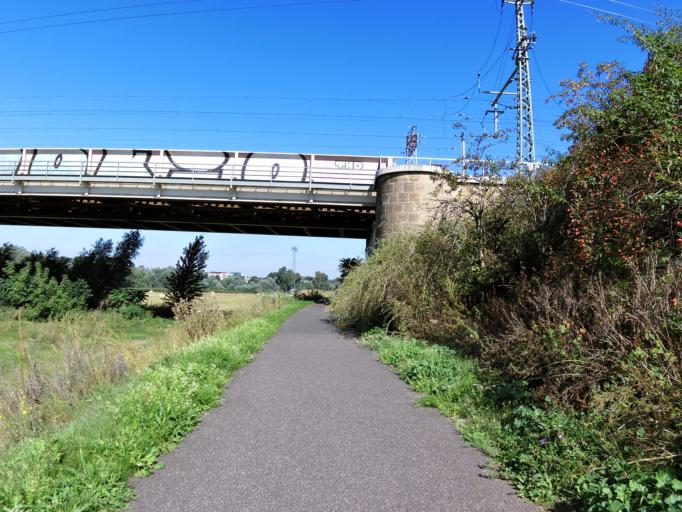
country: DE
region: Saxony
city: Riesa
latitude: 51.3127
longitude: 13.2971
